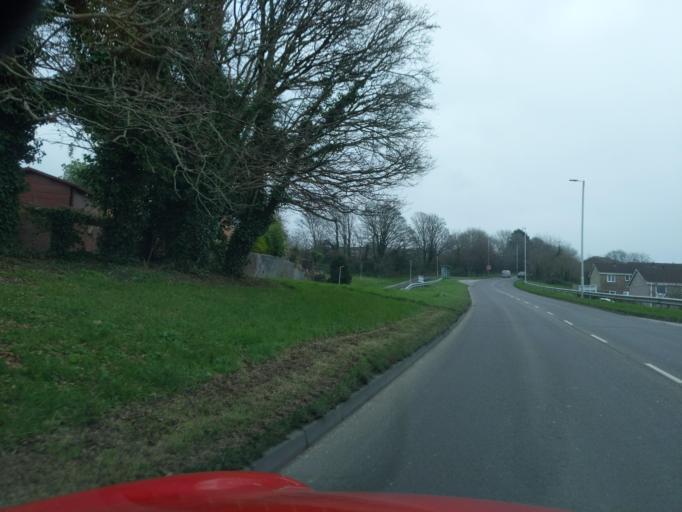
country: GB
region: England
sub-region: Devon
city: Plympton
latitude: 50.3888
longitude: -4.0395
